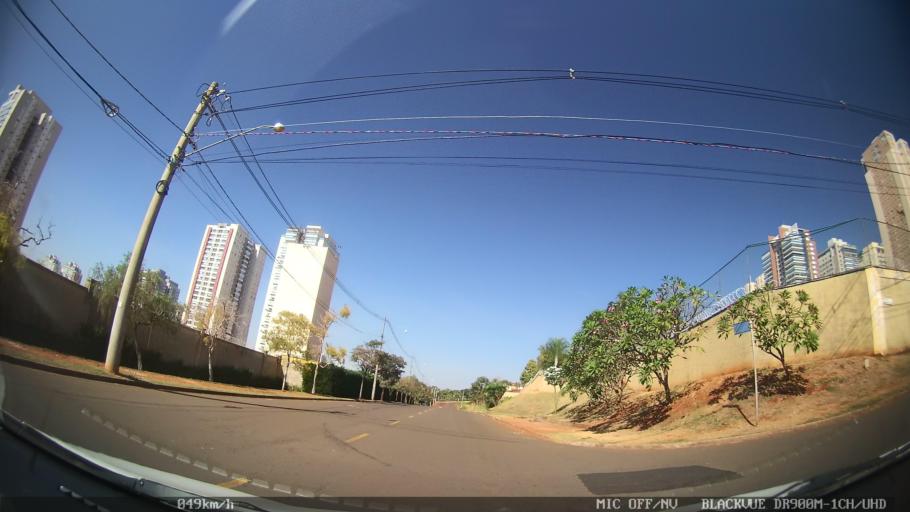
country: BR
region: Sao Paulo
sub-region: Ribeirao Preto
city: Ribeirao Preto
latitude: -21.2164
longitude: -47.8016
